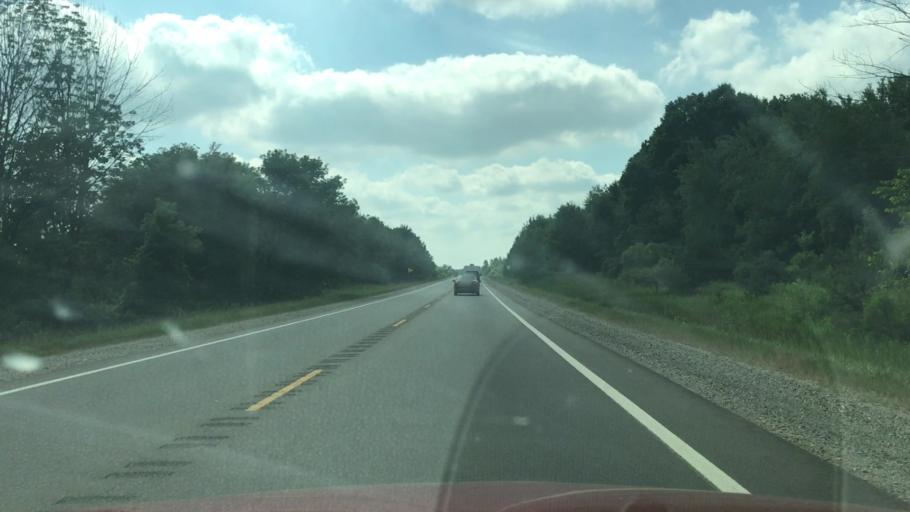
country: US
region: Michigan
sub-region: Kent County
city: Kent City
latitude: 43.2090
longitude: -85.7453
